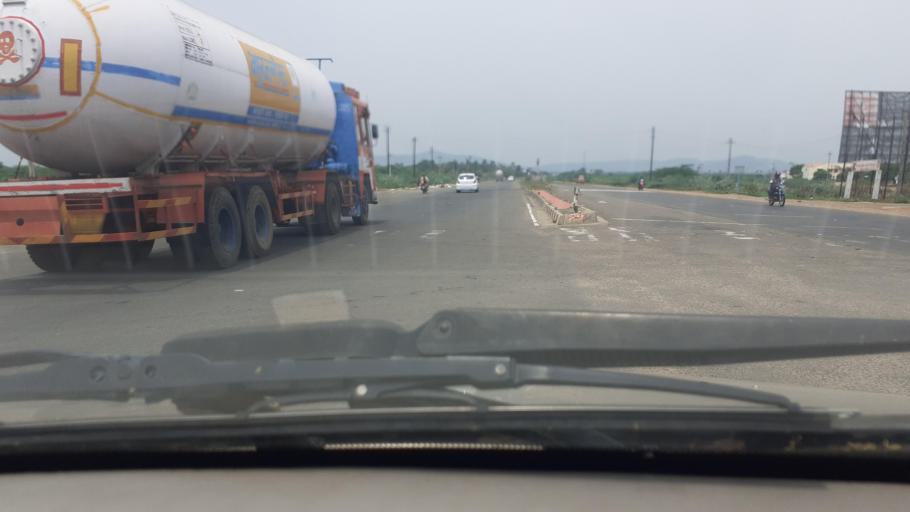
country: IN
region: Tamil Nadu
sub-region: Tirunelveli Kattabo
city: Tirunelveli
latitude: 8.7136
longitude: 77.7907
